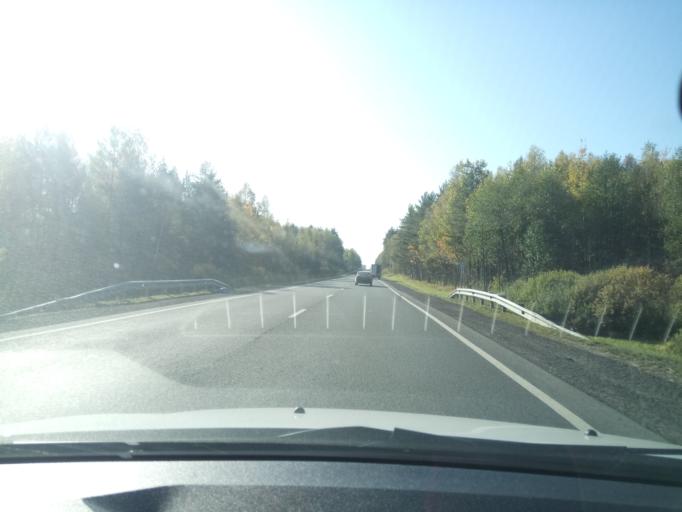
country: RU
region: Nizjnij Novgorod
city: Dal'neye Konstantinovo
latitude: 55.9543
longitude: 43.9767
